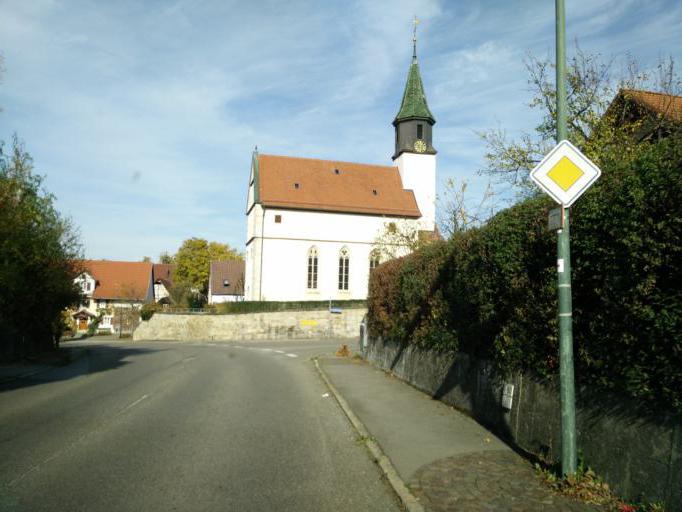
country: DE
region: Baden-Wuerttemberg
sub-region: Tuebingen Region
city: Gomaringen
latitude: 48.4786
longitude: 9.1024
